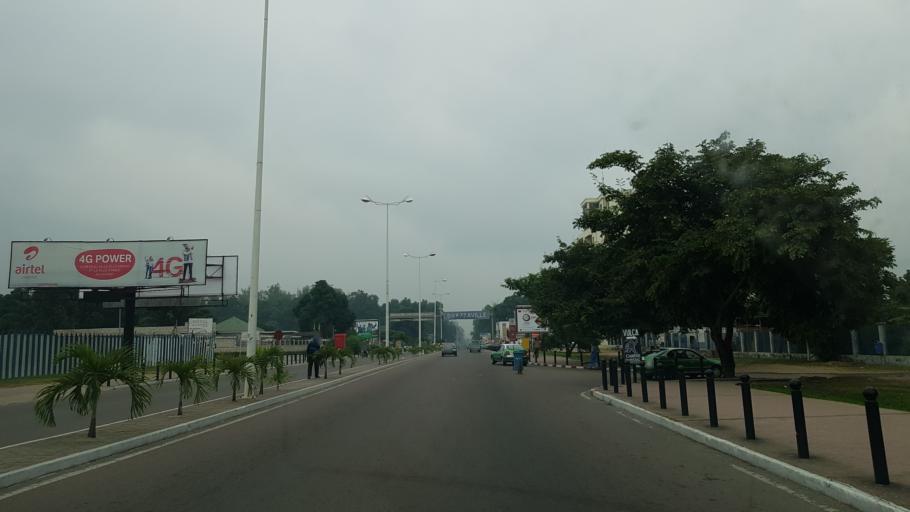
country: CG
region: Brazzaville
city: Brazzaville
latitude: -4.2627
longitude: 15.2524
